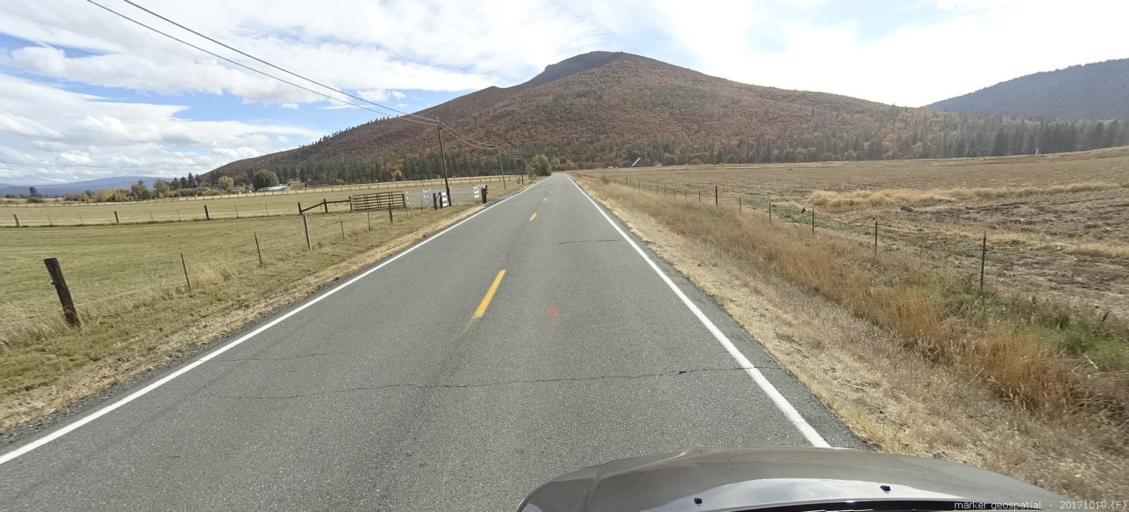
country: US
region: California
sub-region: Shasta County
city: Burney
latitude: 41.0426
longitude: -121.4947
